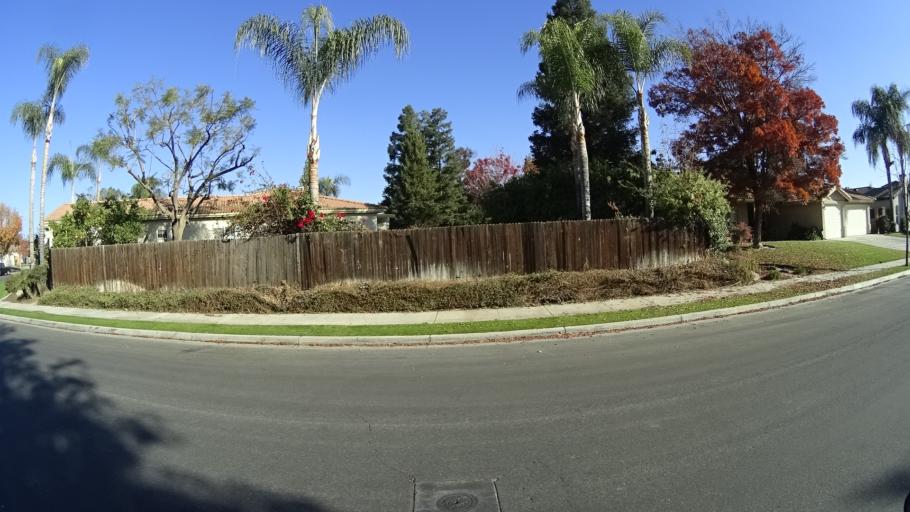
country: US
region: California
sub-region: Kern County
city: Rosedale
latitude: 35.3273
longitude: -119.1331
